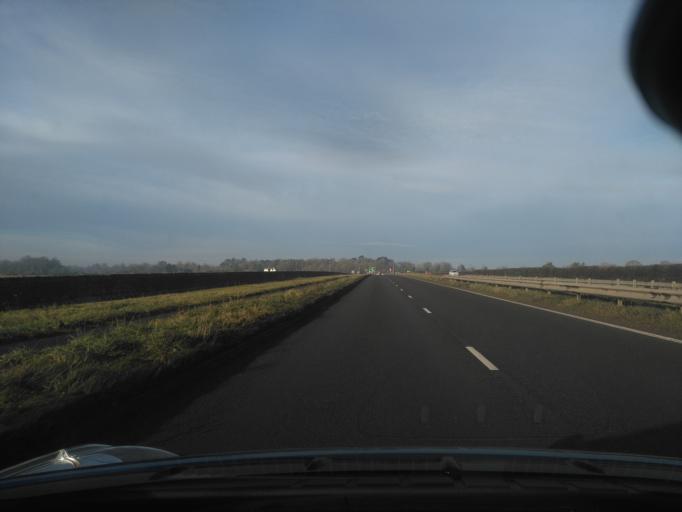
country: GB
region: England
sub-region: Oxfordshire
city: Woodstock
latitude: 51.8341
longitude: -1.3288
